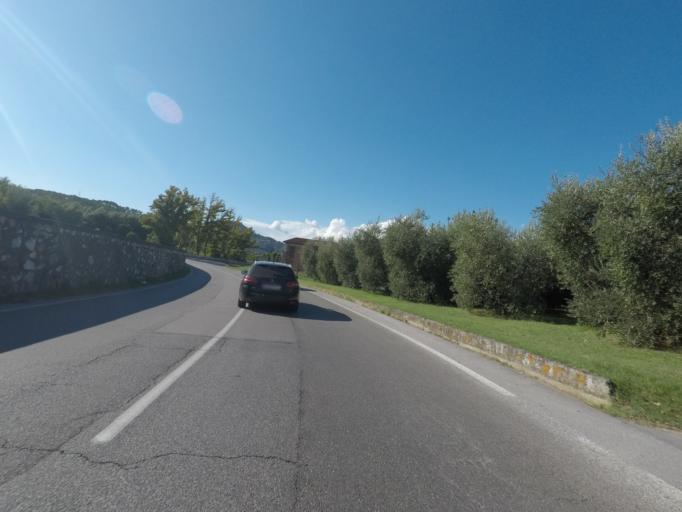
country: IT
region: Tuscany
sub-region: Provincia di Lucca
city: Lucca
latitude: 43.8750
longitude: 10.4918
